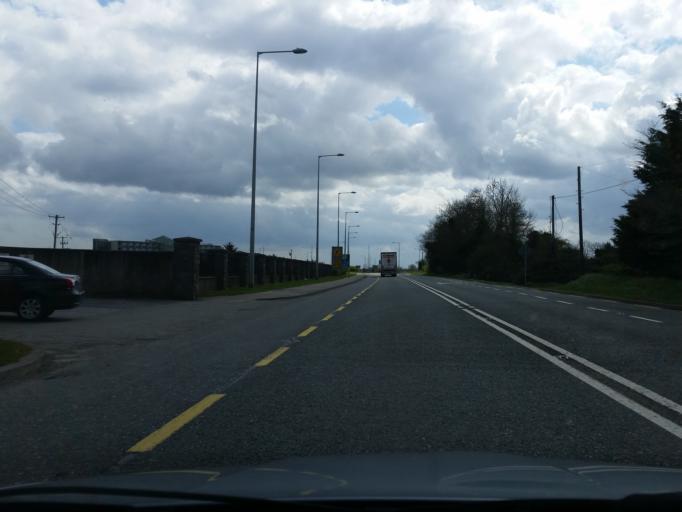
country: IE
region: Leinster
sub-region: An Mhi
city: Ashbourne
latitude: 53.5293
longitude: -6.4189
